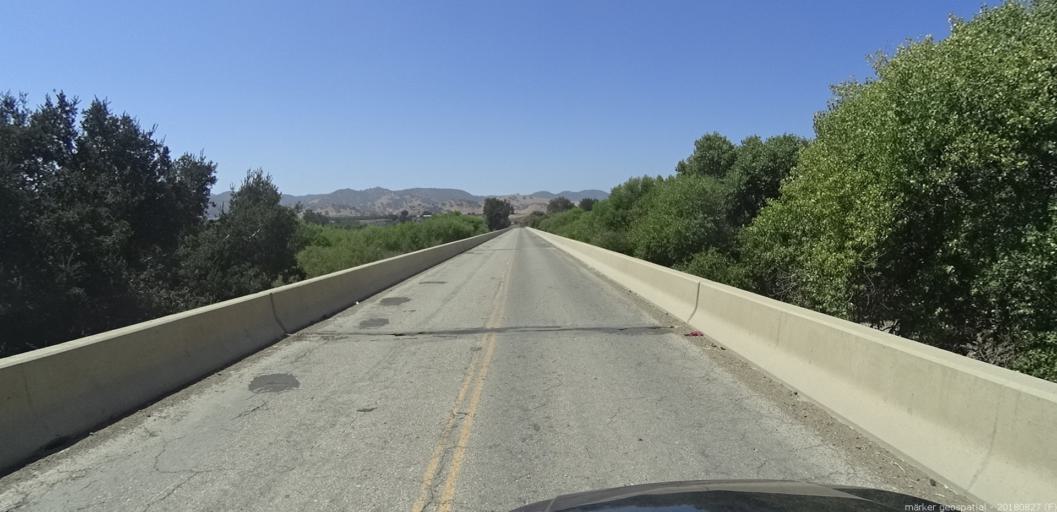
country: US
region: California
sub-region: Monterey County
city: King City
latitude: 36.0171
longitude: -120.9115
